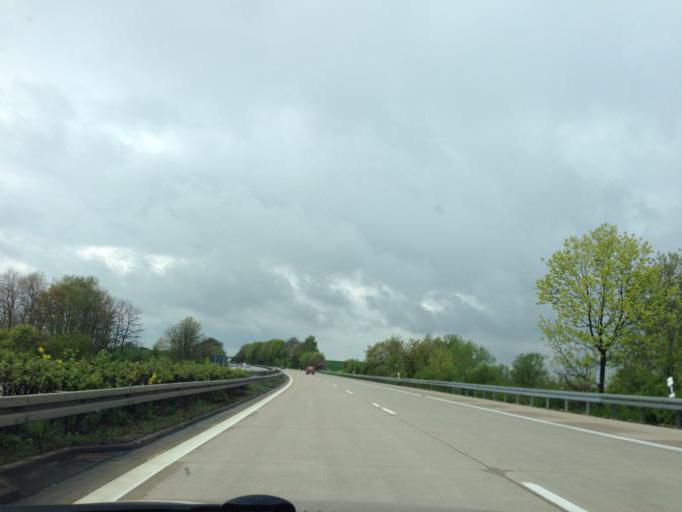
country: DE
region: Saxony
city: Nerchau
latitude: 51.2528
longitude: 12.8330
